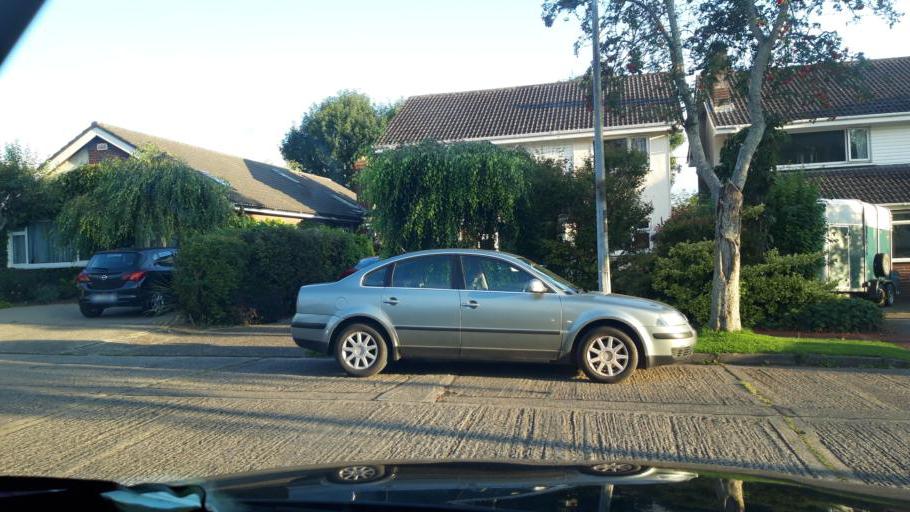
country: IE
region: Leinster
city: Malahide
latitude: 53.4454
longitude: -6.1543
